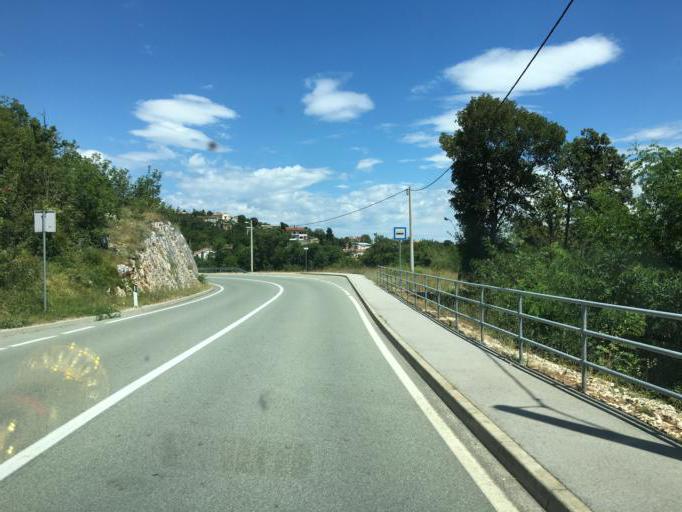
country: HR
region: Istarska
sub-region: Grad Labin
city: Rabac
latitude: 45.1607
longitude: 14.2192
